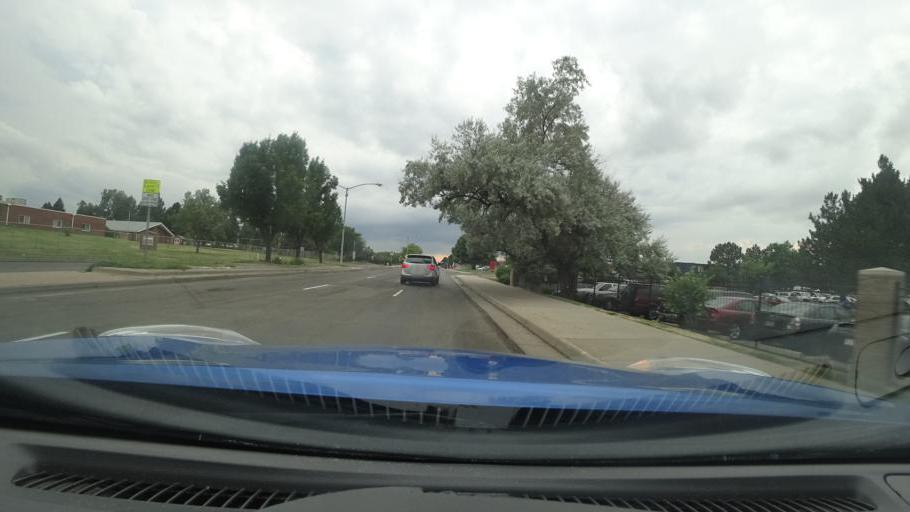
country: US
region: Colorado
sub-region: Adams County
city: Aurora
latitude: 39.6967
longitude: -104.8160
